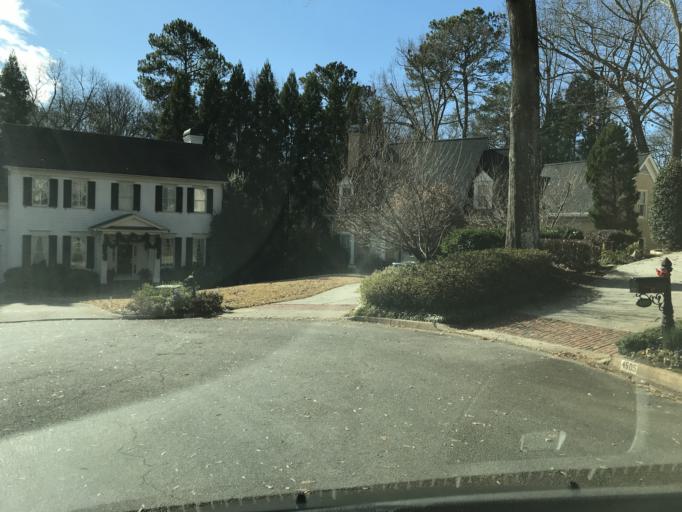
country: US
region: Georgia
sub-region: DeKalb County
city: North Atlanta
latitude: 33.8835
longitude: -84.3515
